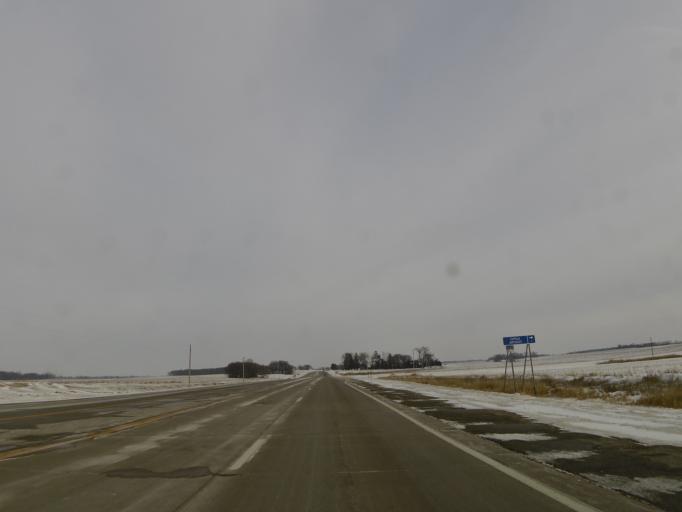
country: US
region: Minnesota
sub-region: McLeod County
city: Hutchinson
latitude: 44.8925
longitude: -94.2560
